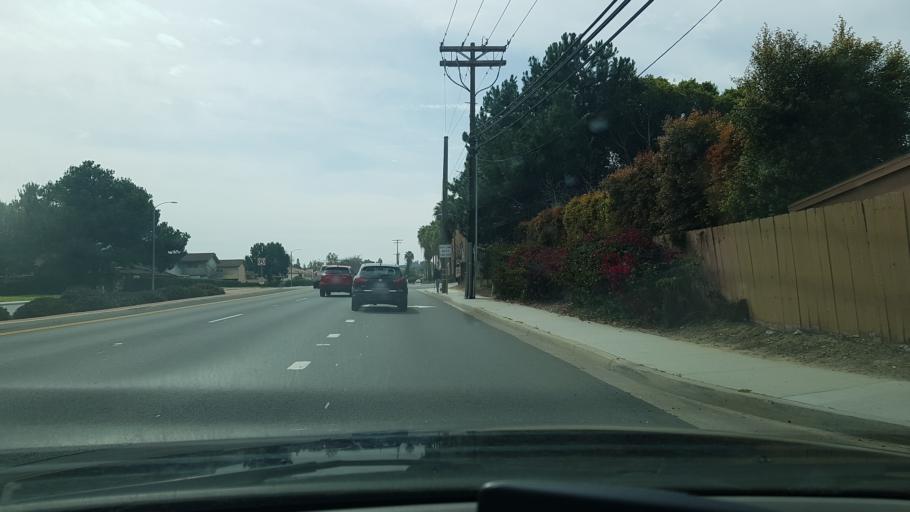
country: US
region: California
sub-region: San Diego County
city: Lake San Marcos
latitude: 33.1381
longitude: -117.2045
